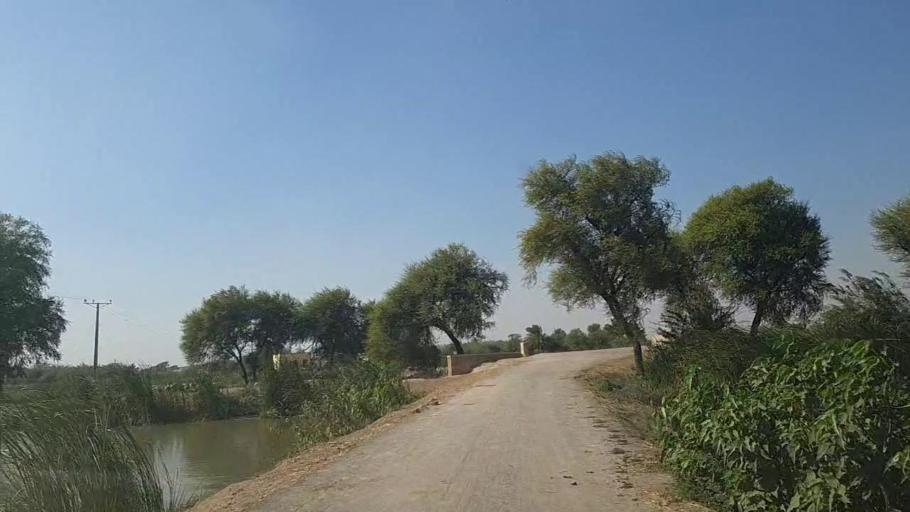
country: PK
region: Sindh
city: Daro Mehar
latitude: 24.9734
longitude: 68.1256
